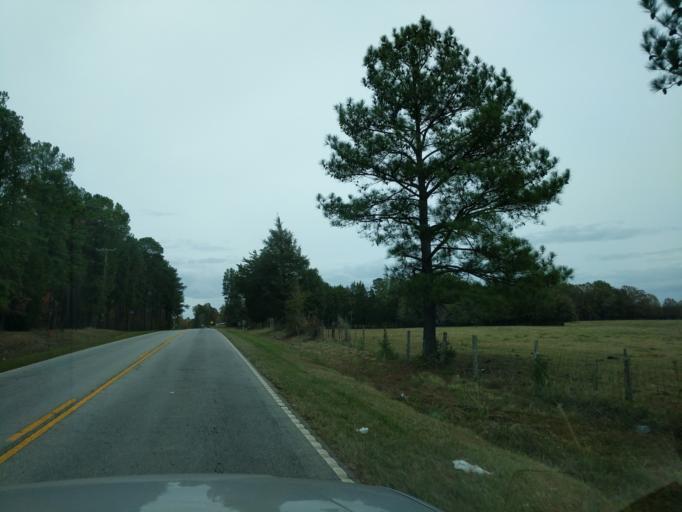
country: US
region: South Carolina
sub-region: Saluda County
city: Saluda
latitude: 34.0710
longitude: -81.7603
